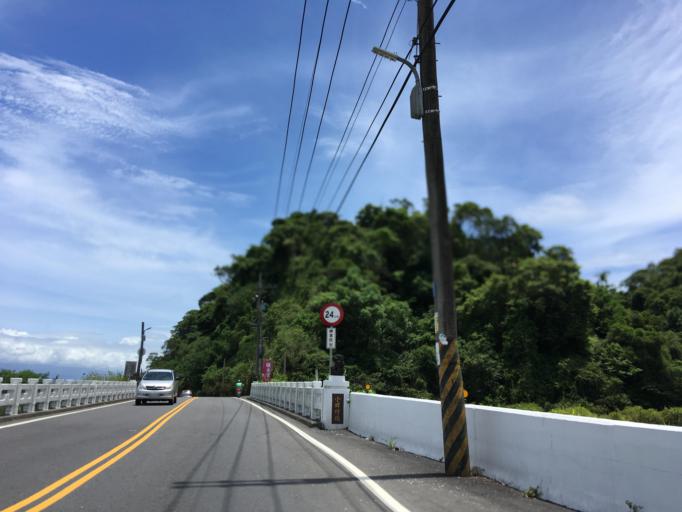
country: TW
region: Taiwan
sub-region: Yilan
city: Yilan
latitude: 24.6439
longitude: 121.7220
